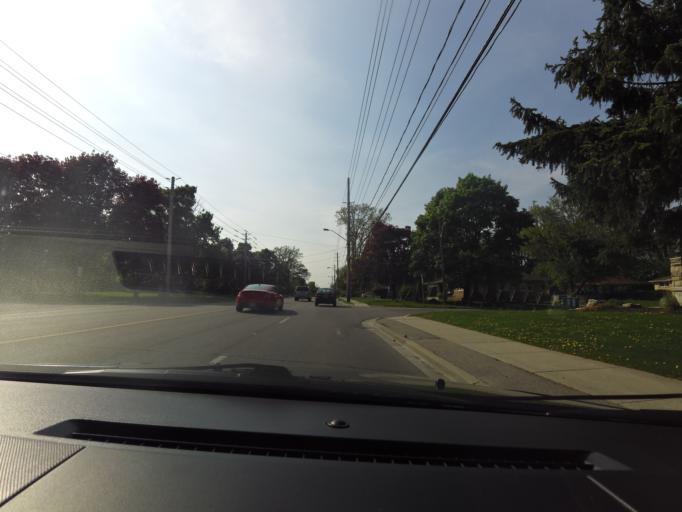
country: CA
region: Ontario
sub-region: Wellington County
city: Guelph
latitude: 43.5259
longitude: -80.2422
